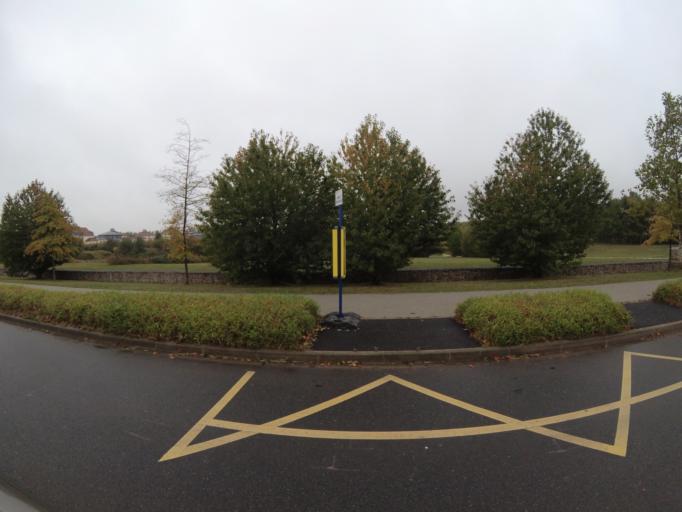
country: FR
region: Ile-de-France
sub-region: Departement de Seine-et-Marne
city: Conches-sur-Gondoire
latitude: 48.8370
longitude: 2.7220
